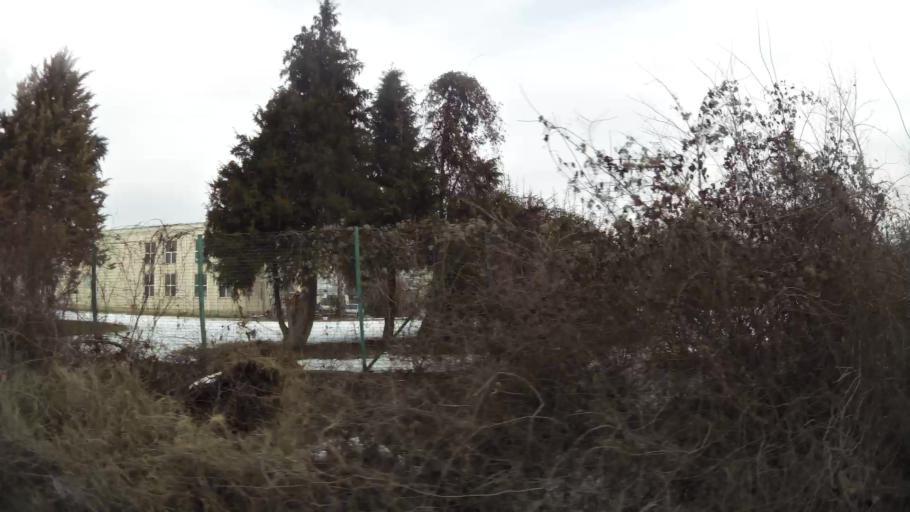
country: MK
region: Suto Orizari
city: Suto Orizare
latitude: 42.0326
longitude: 21.4032
